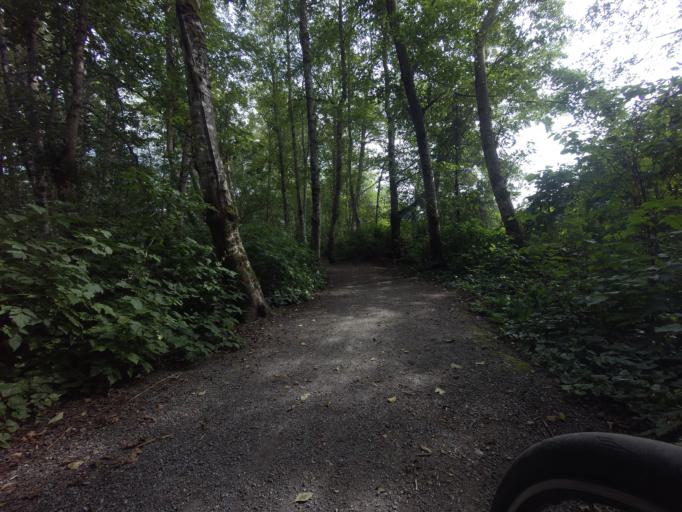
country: CA
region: British Columbia
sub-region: Greater Vancouver Regional District
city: Lions Bay
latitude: 49.7055
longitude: -123.1473
